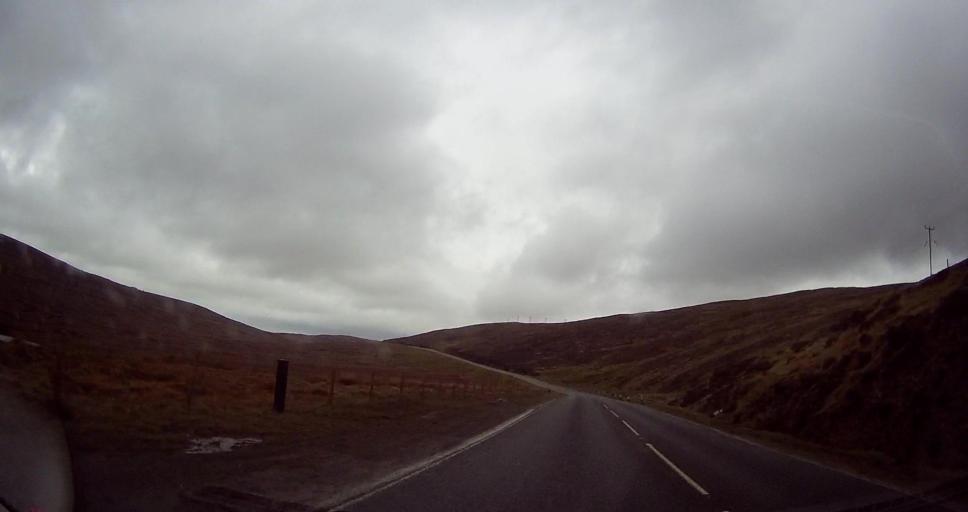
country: GB
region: Scotland
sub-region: Shetland Islands
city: Lerwick
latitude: 60.3152
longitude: -1.2471
